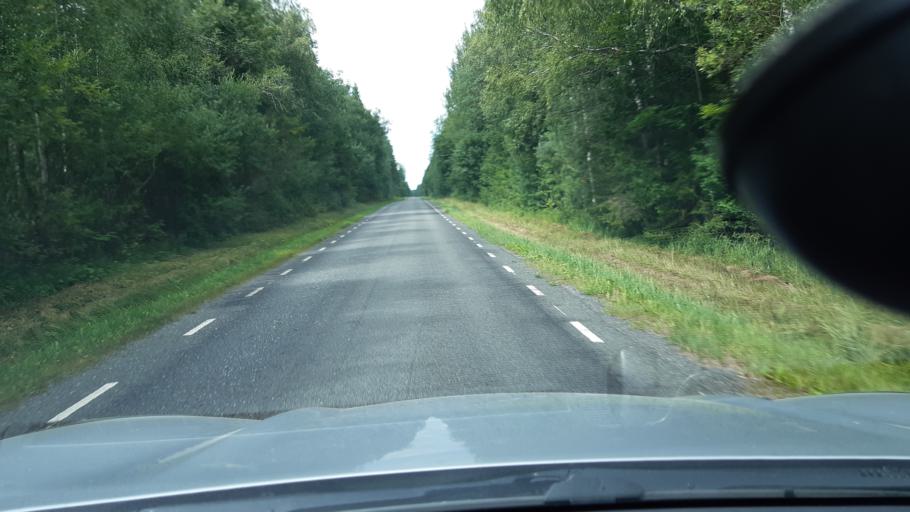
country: EE
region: Raplamaa
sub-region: Jaervakandi vald
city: Jarvakandi
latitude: 58.8634
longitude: 24.7816
